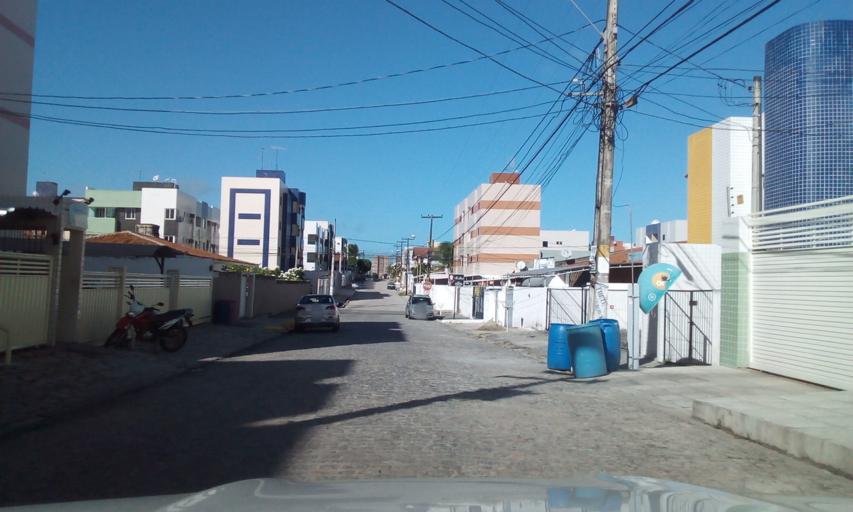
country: BR
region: Paraiba
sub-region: Joao Pessoa
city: Joao Pessoa
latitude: -7.1554
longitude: -34.8366
